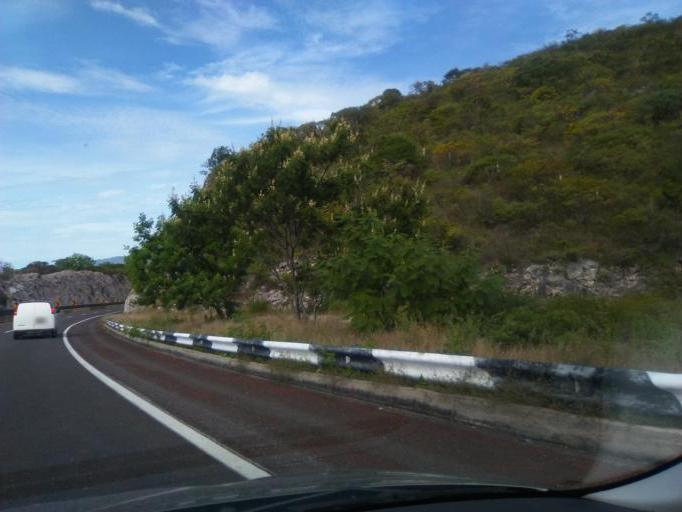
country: MX
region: Guerrero
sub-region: Eduardo Neri
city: Tlanipatla
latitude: 17.8627
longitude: -99.4061
